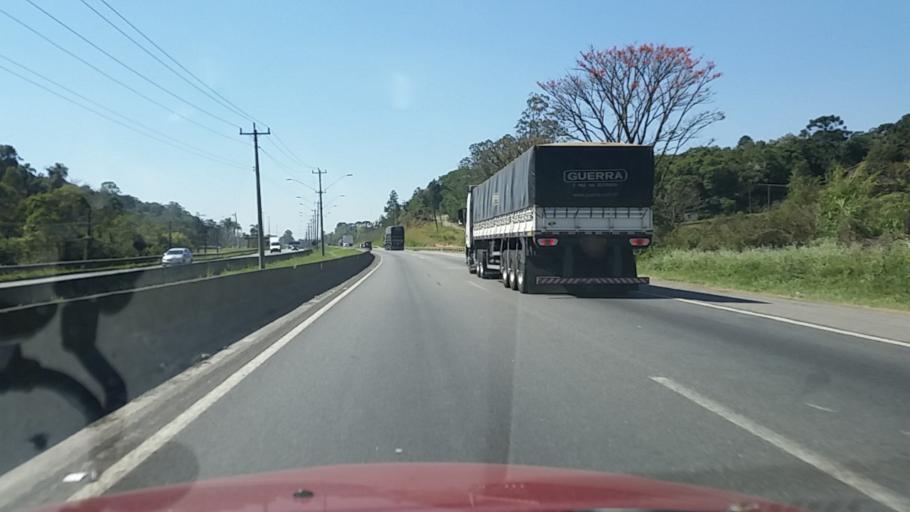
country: BR
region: Sao Paulo
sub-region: Itapecerica Da Serra
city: Itapecerica da Serra
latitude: -23.7716
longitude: -46.9119
